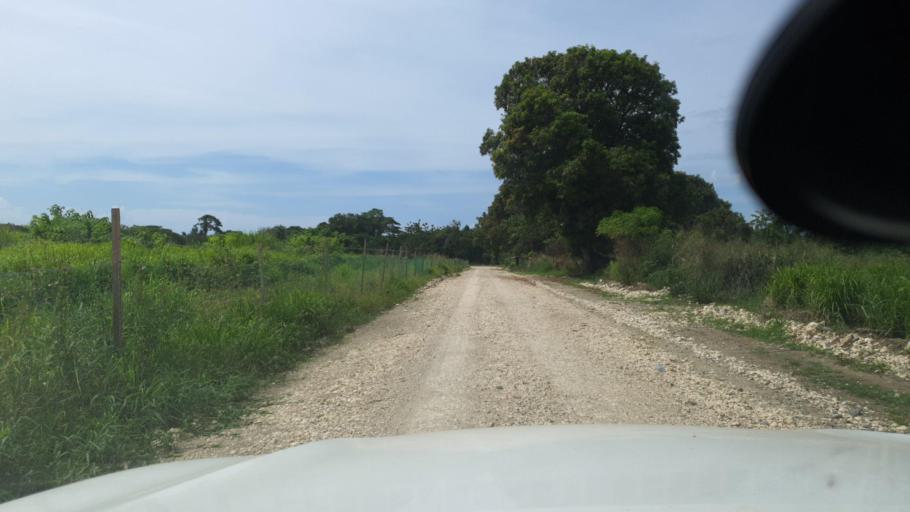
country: SB
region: Guadalcanal
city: Honiara
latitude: -9.4146
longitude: 159.8915
